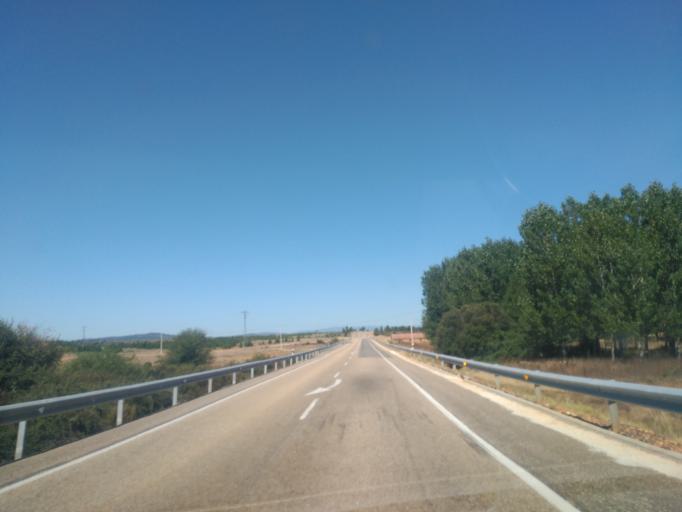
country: ES
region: Castille and Leon
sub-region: Provincia de Zamora
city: Otero de Bodas
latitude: 41.9420
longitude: -6.1796
